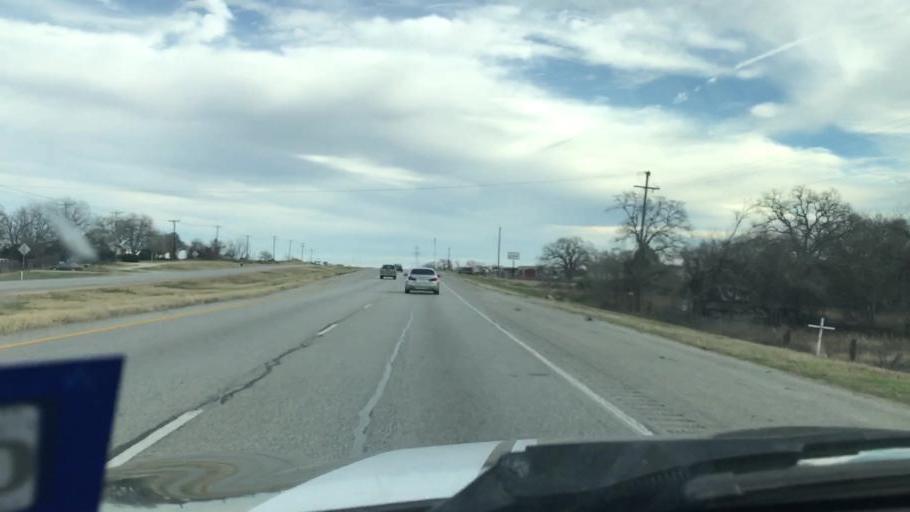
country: US
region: Texas
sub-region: Bastrop County
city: Elgin
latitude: 30.3339
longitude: -97.3586
